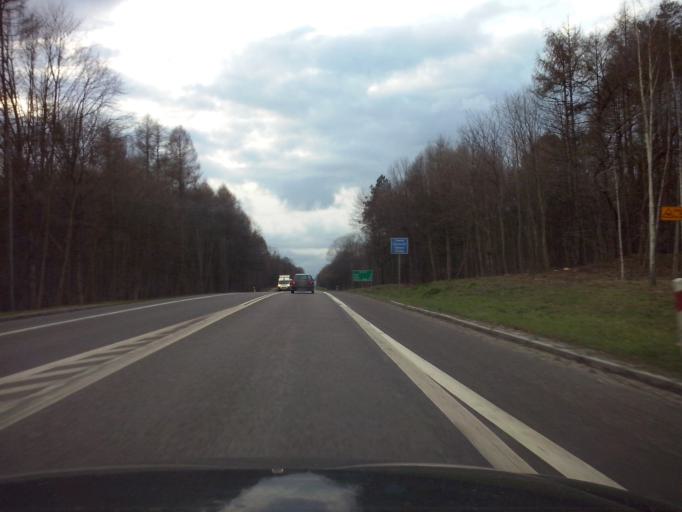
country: PL
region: Lublin Voivodeship
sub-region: Chelm
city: Chelm
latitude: 51.1501
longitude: 23.4254
